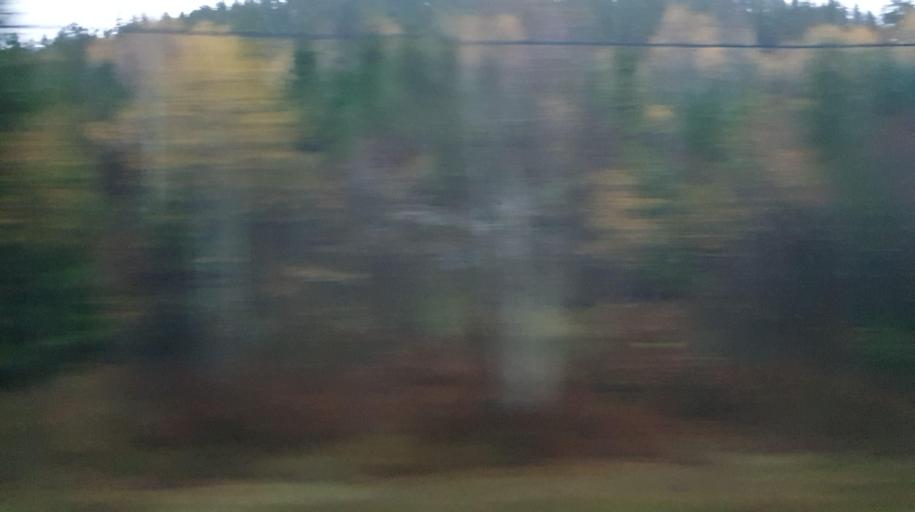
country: NO
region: Buskerud
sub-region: Krodsherad
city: Noresund
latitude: 60.1489
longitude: 9.7610
